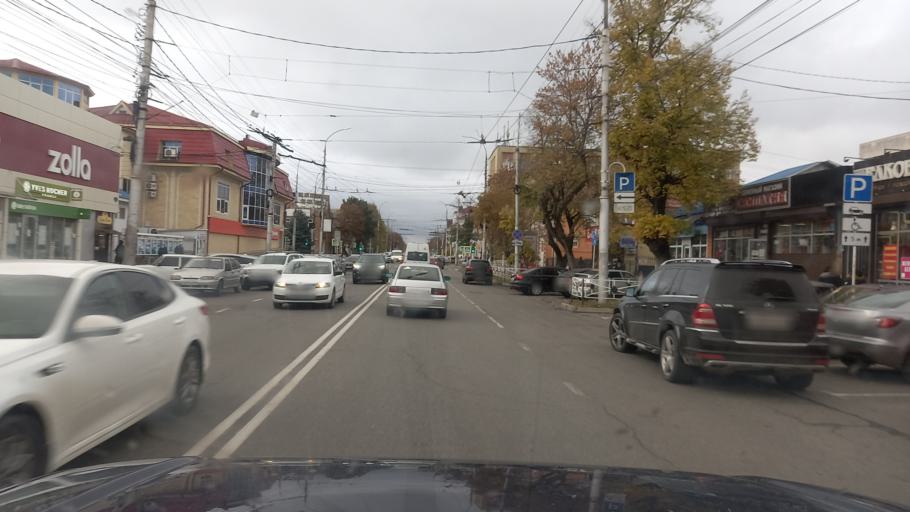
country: RU
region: Adygeya
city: Maykop
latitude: 44.6089
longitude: 40.1087
